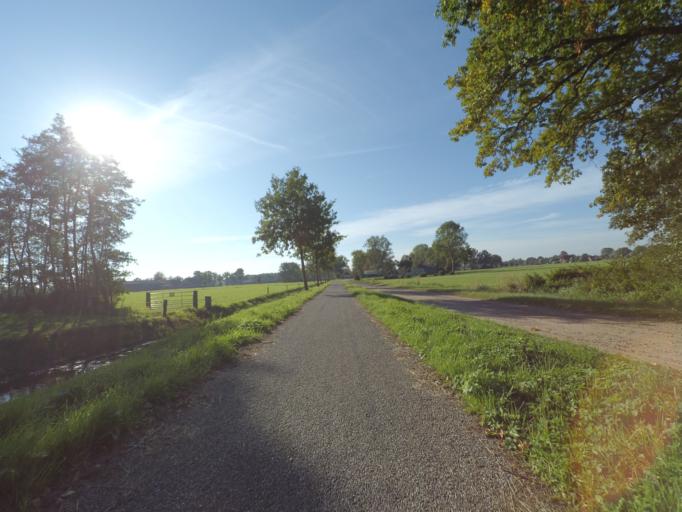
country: NL
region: Gelderland
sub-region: Gemeente Nijkerk
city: Nijkerk
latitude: 52.2353
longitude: 5.5266
